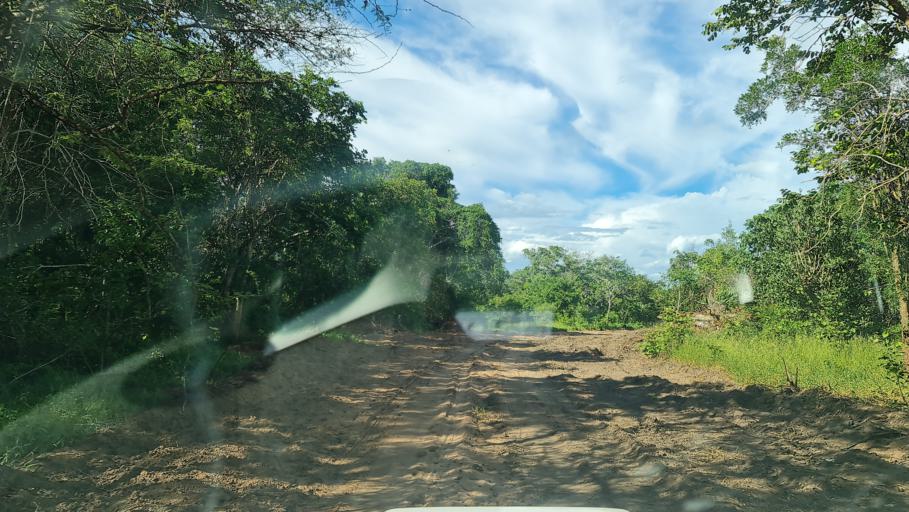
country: MZ
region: Nampula
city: Antonio Enes
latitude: -15.5124
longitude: 40.1316
